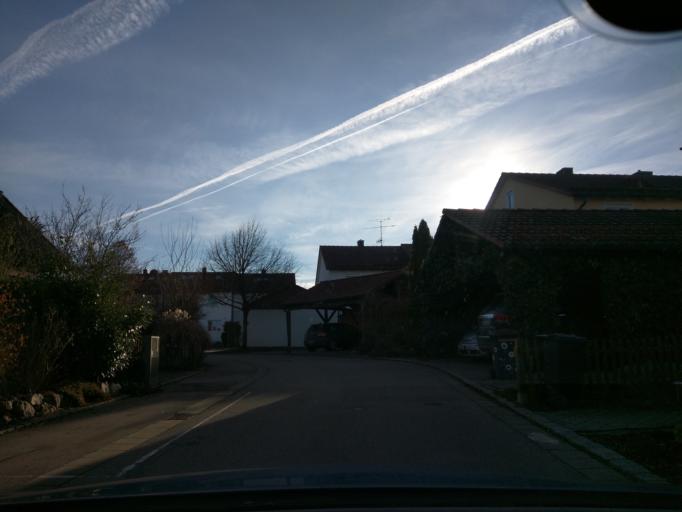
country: DE
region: Bavaria
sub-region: Upper Bavaria
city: Au in der Hallertau
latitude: 48.5528
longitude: 11.7395
